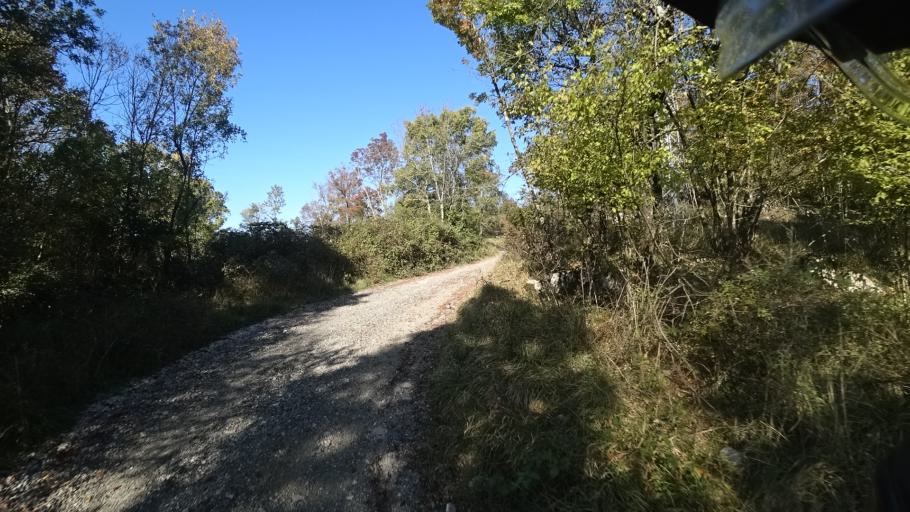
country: HR
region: Primorsko-Goranska
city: Klana
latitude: 45.4236
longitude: 14.3432
